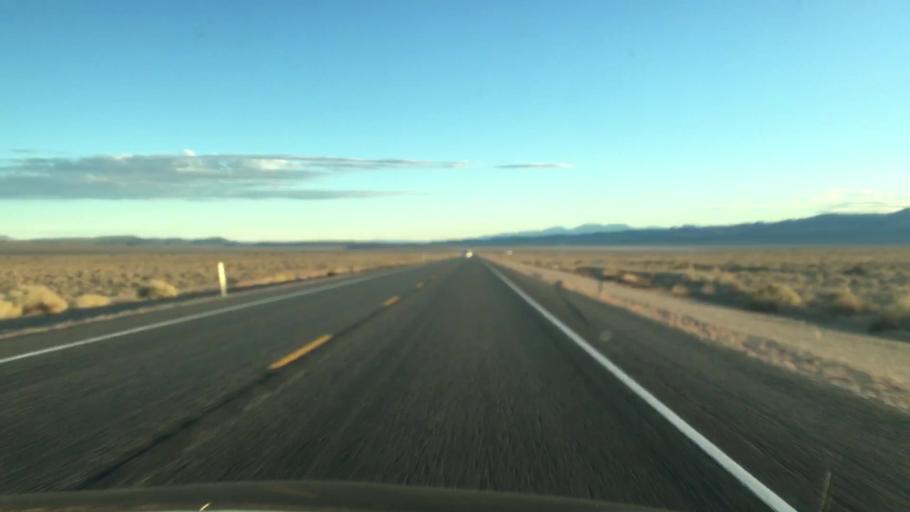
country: US
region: Nevada
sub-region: Esmeralda County
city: Goldfield
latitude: 37.5238
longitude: -117.1906
